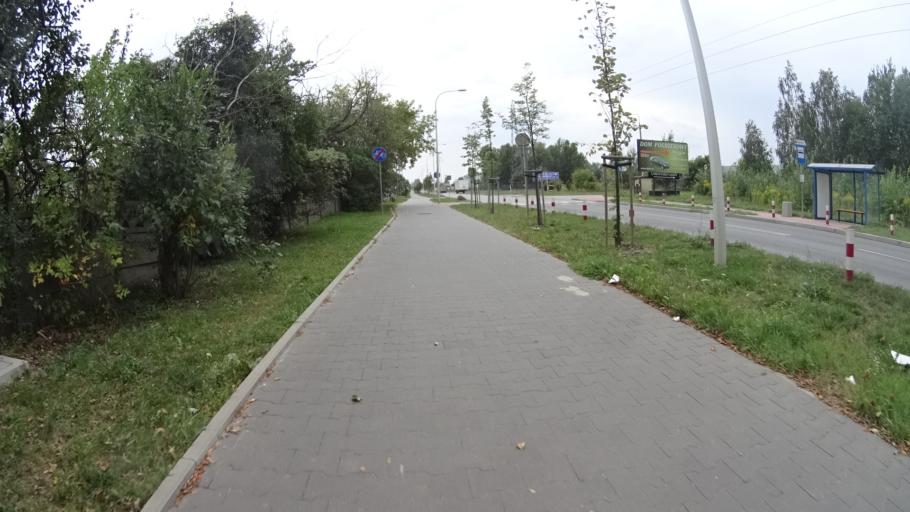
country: PL
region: Masovian Voivodeship
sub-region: Powiat pruszkowski
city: Otrebusy
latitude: 52.1662
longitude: 20.7681
